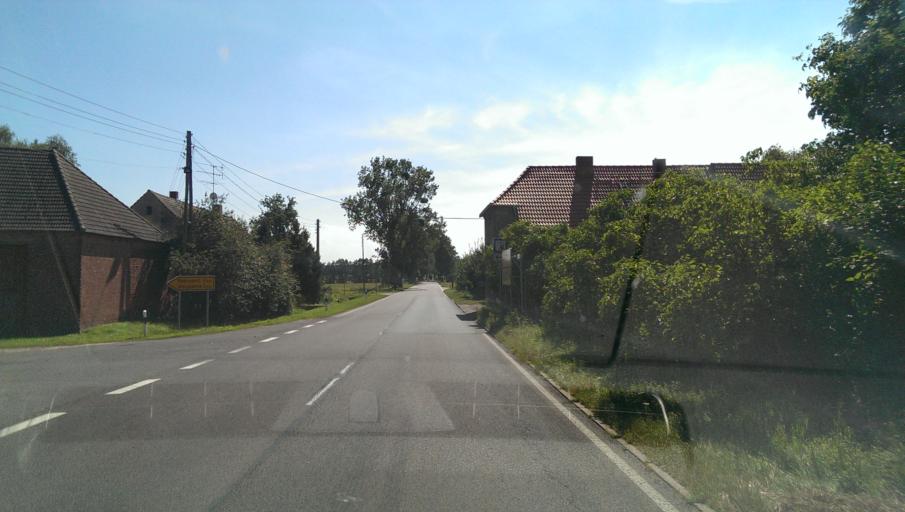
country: DE
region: Saxony-Anhalt
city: Kropstadt
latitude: 51.9678
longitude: 12.7554
